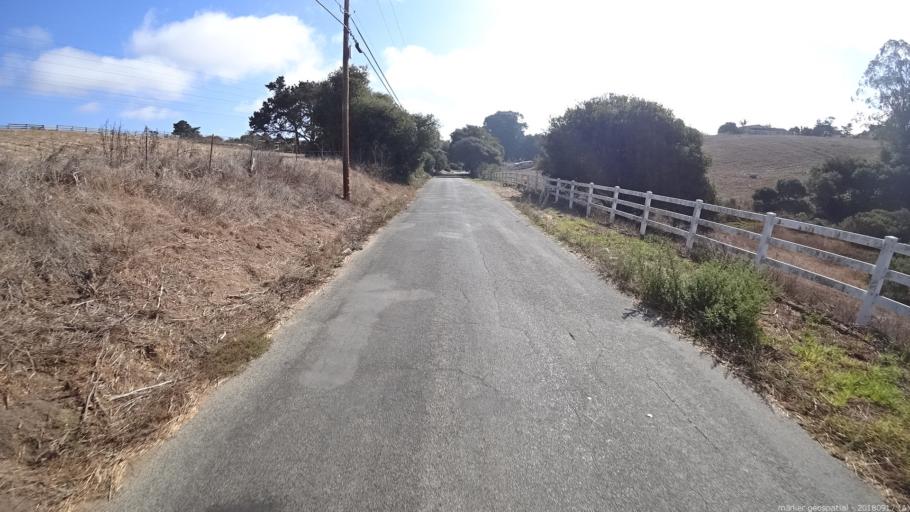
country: US
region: California
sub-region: Monterey County
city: Elkhorn
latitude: 36.7918
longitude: -121.7163
